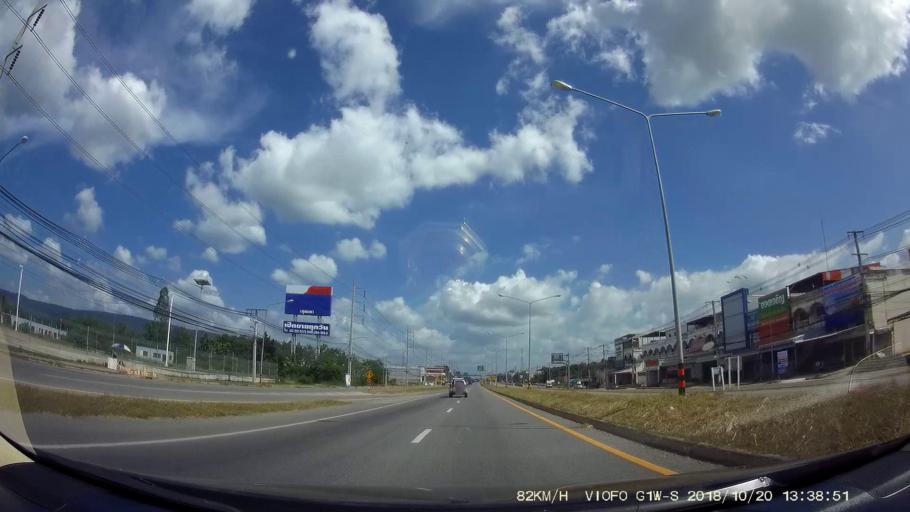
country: TH
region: Khon Kaen
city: Chum Phae
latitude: 16.5509
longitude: 102.0868
